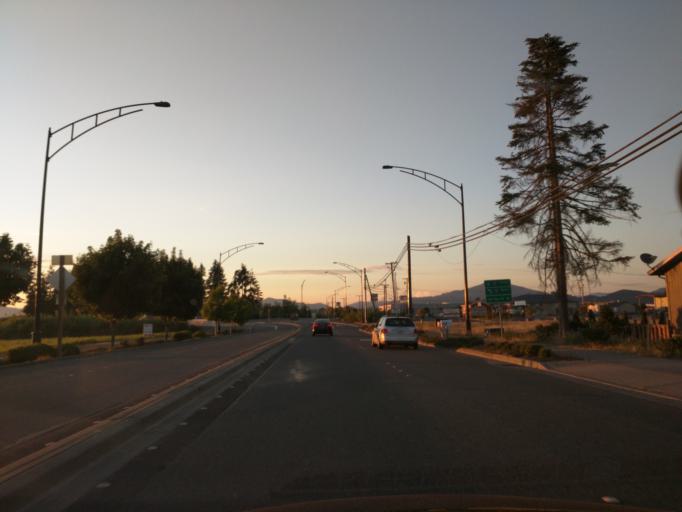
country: US
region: Washington
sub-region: Skagit County
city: Burlington
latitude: 48.4821
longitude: -122.3354
